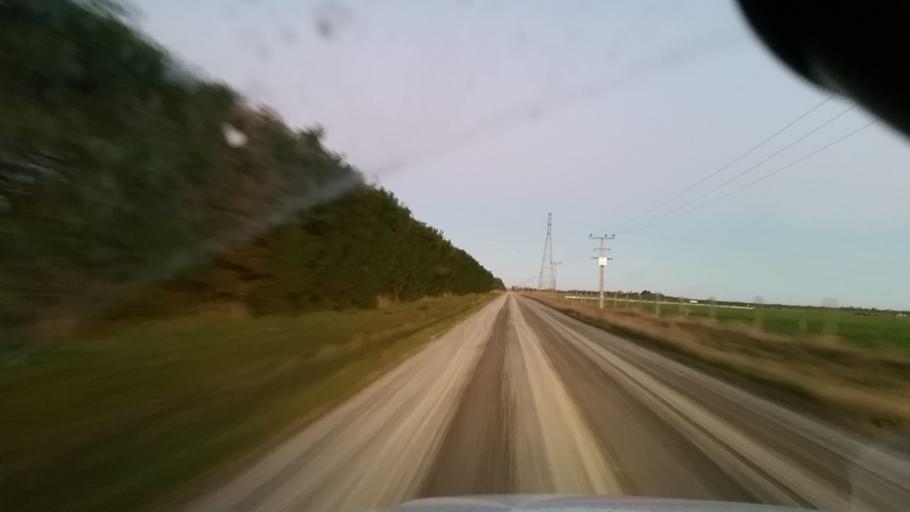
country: NZ
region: Canterbury
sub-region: Ashburton District
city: Tinwald
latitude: -43.9812
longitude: 171.6478
